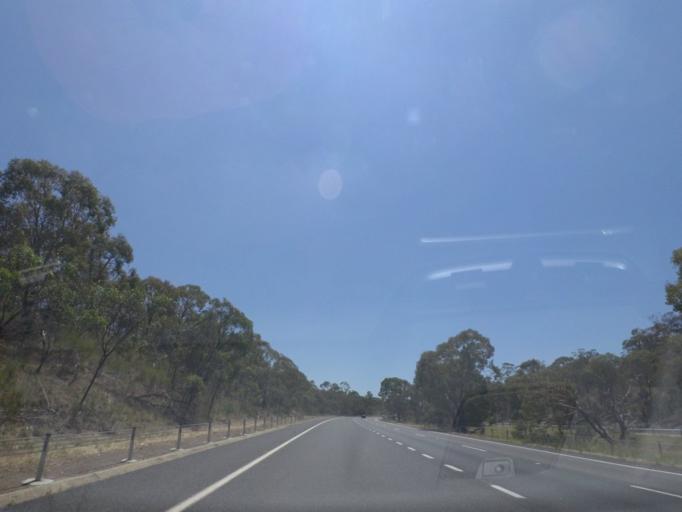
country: AU
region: Victoria
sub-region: Murrindindi
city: Kinglake West
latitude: -36.9611
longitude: 145.1841
